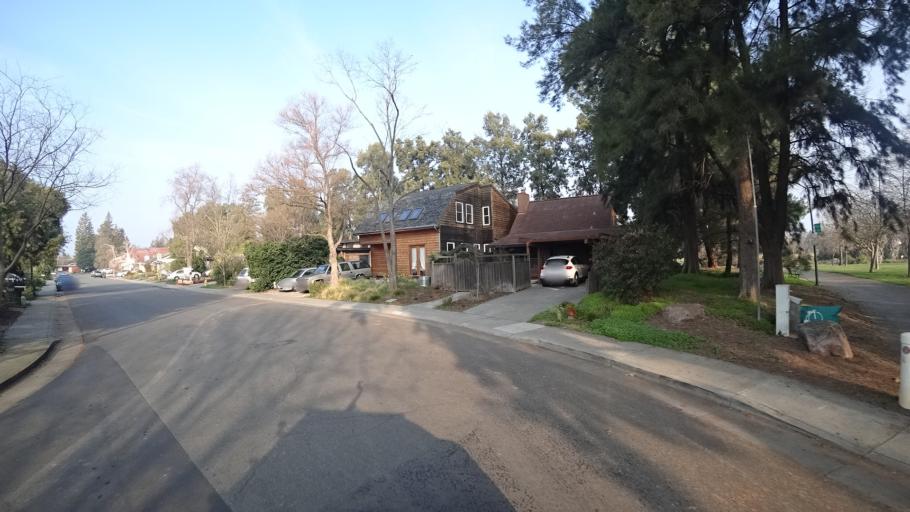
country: US
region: California
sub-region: Yolo County
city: Davis
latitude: 38.5704
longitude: -121.7515
